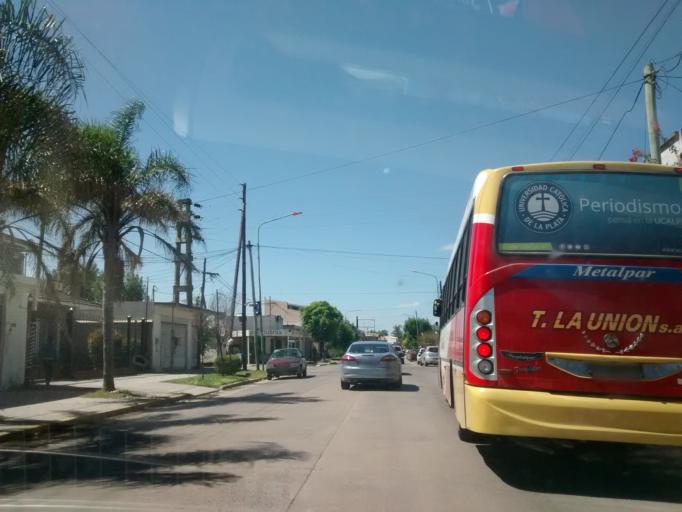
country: AR
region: Buenos Aires
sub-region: Partido de Berisso
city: Berisso
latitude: -34.8781
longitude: -57.8515
